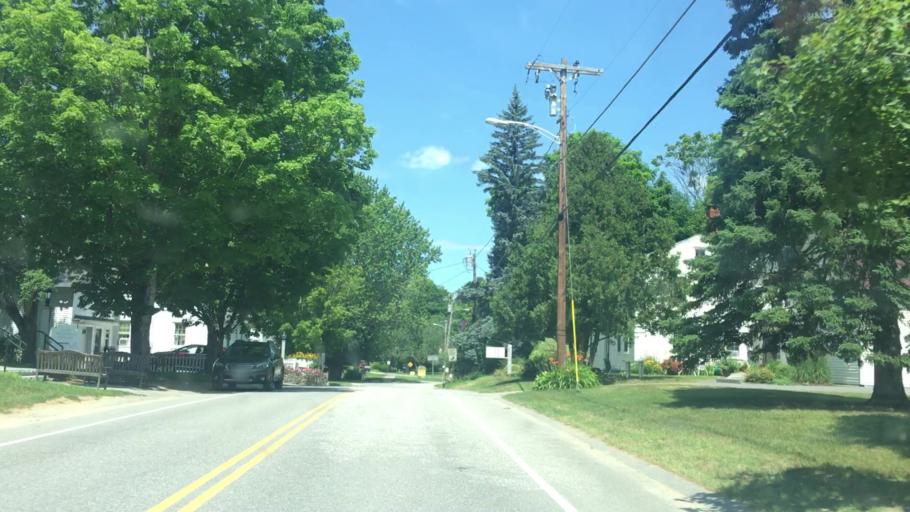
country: US
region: Maine
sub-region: Kennebec County
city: Wayne
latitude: 44.3471
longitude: -70.0656
